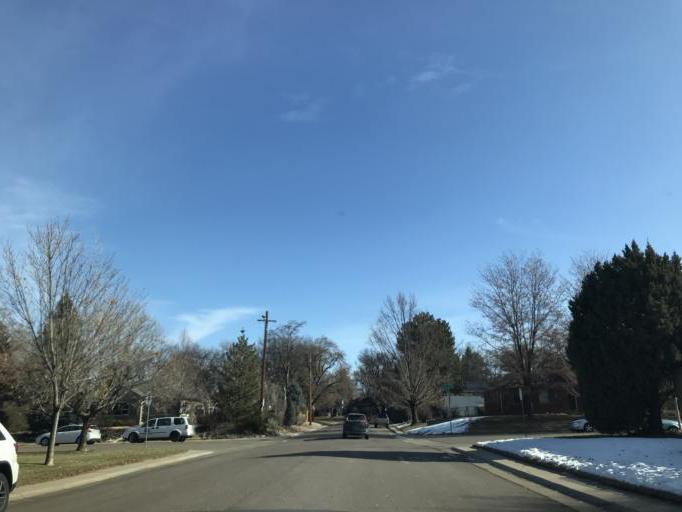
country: US
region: Colorado
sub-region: Arapahoe County
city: Glendale
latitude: 39.7351
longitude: -104.9145
